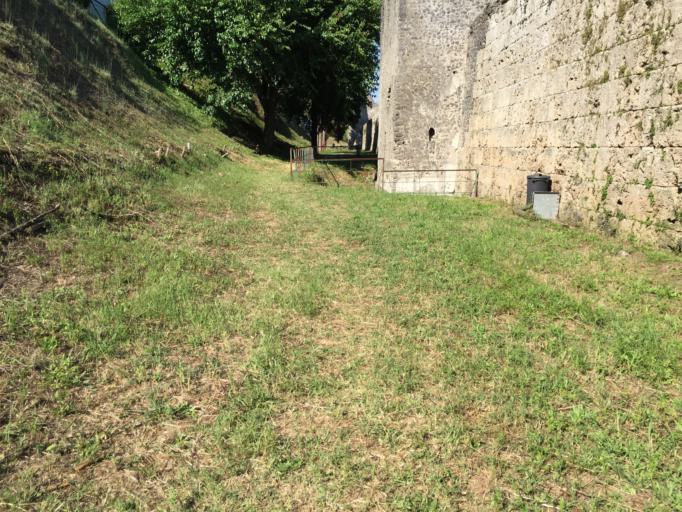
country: IT
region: Campania
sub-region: Provincia di Napoli
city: Pompei
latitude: 40.7527
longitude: 14.4826
